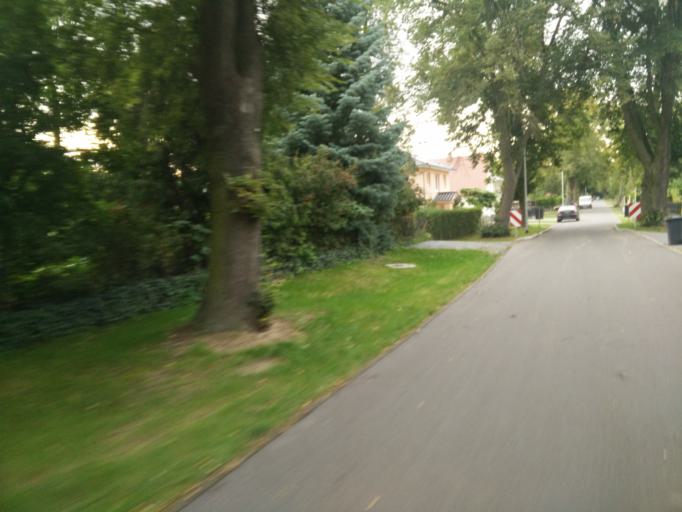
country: DE
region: Brandenburg
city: Falkensee
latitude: 52.5751
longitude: 13.0873
